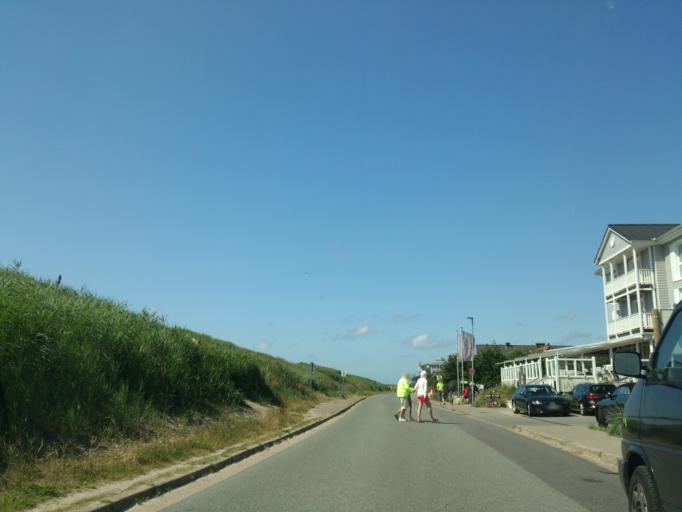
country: DE
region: Schleswig-Holstein
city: Sankt Peter-Ording
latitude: 54.3330
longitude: 8.6054
